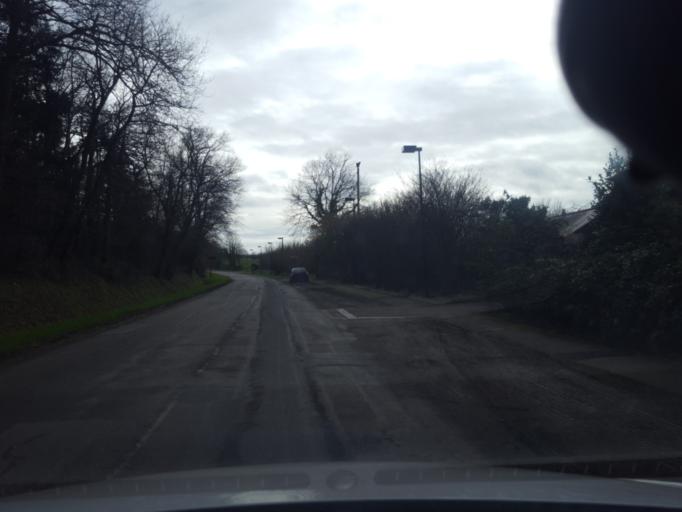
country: FR
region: Brittany
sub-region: Departement d'Ille-et-Vilaine
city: Guignen
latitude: 47.9167
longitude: -1.8613
